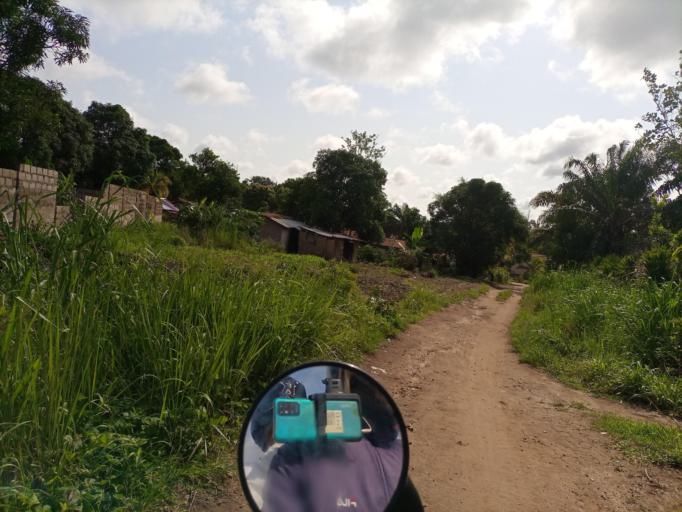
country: SL
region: Southern Province
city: Bo
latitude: 7.9618
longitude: -11.7643
